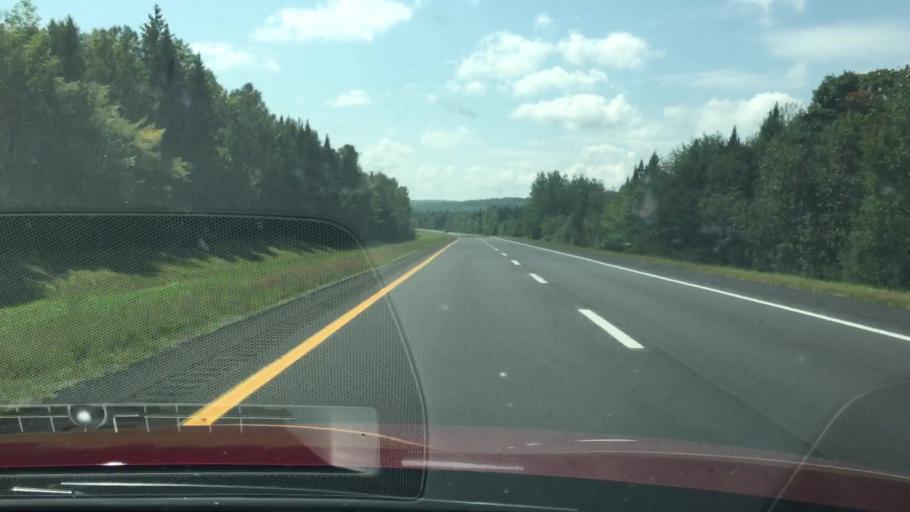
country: US
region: Maine
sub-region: Penobscot County
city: Patten
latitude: 45.8976
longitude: -68.3955
